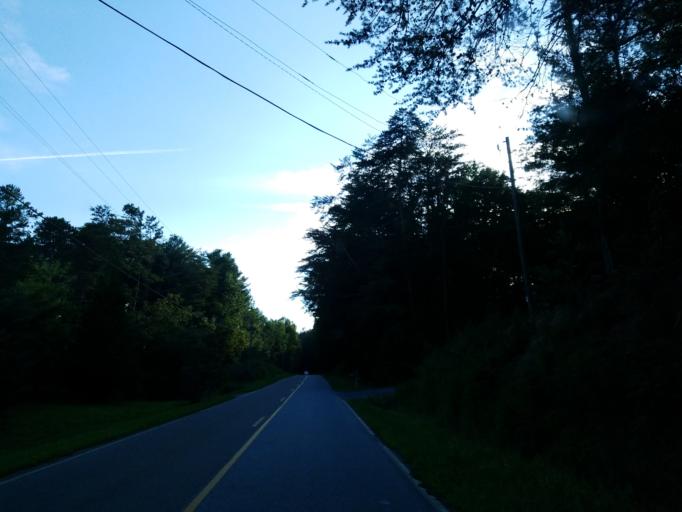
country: US
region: Georgia
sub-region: Gilmer County
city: Ellijay
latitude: 34.6018
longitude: -84.4032
